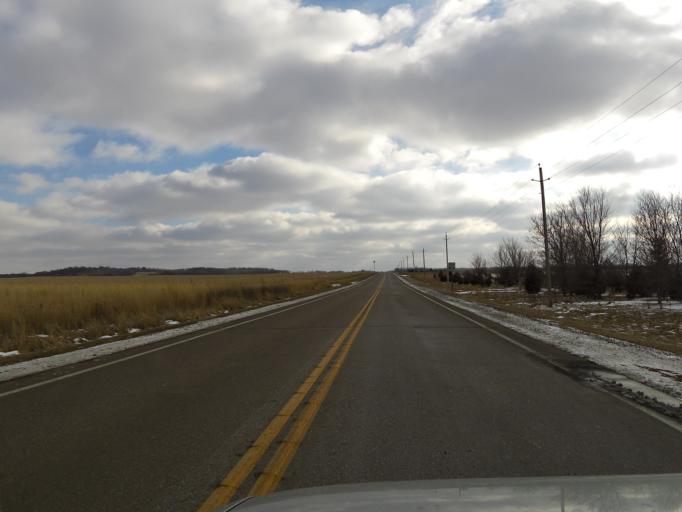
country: US
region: Minnesota
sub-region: Scott County
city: Prior Lake
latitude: 44.7704
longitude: -93.4494
